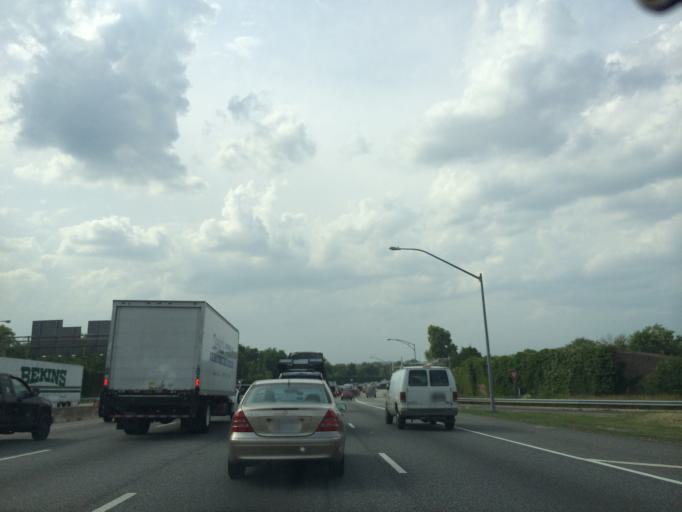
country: US
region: Maryland
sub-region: Baltimore County
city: Catonsville
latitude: 39.2881
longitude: -76.7403
